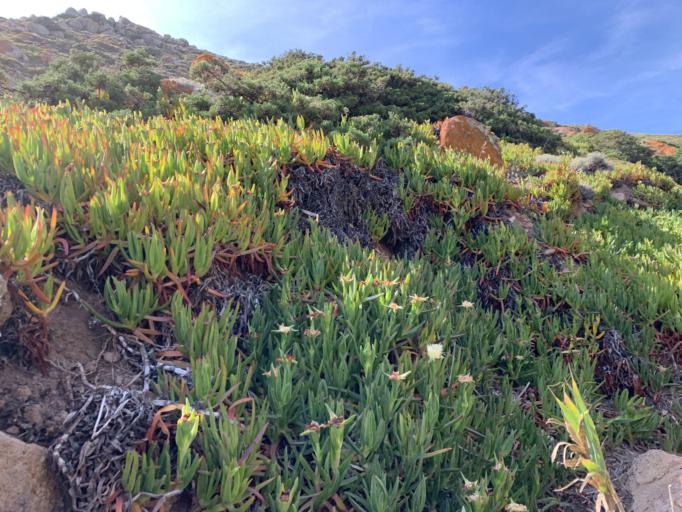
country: PT
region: Lisbon
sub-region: Sintra
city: Colares
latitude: 38.7774
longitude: -9.4968
